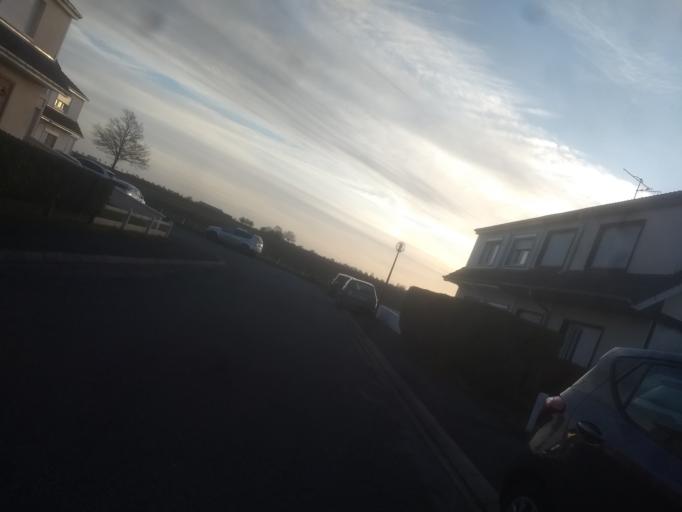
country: FR
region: Nord-Pas-de-Calais
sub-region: Departement du Pas-de-Calais
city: Agny
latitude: 50.2650
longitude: 2.7730
